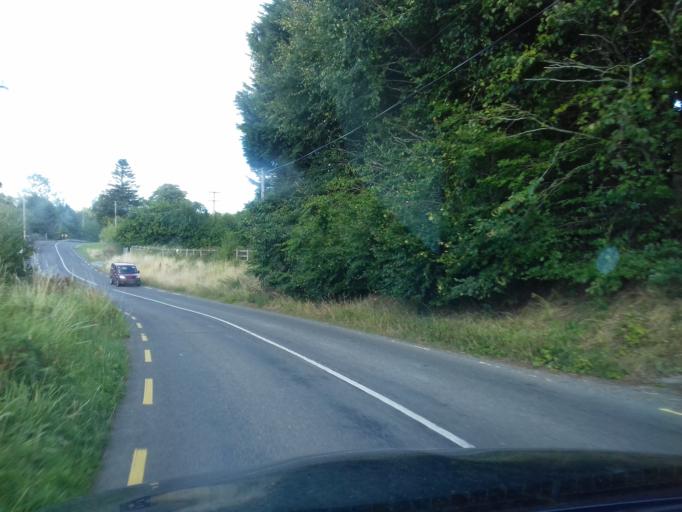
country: IE
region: Leinster
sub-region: Kilkenny
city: Thomastown
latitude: 52.5355
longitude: -7.1065
